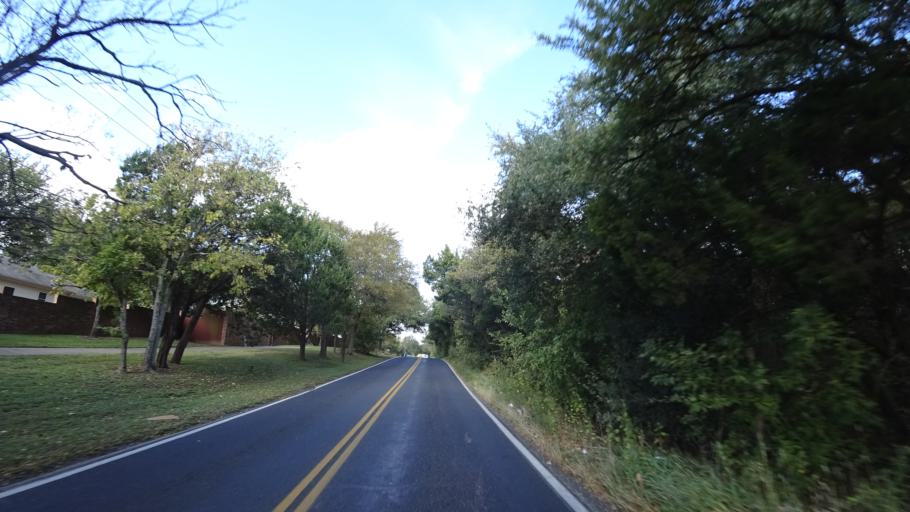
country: US
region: Texas
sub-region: Travis County
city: Manchaca
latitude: 30.1867
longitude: -97.8179
